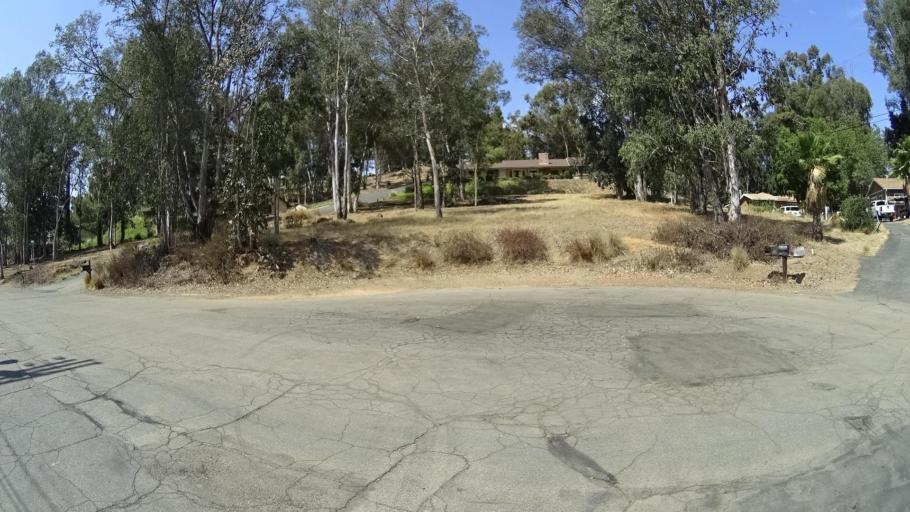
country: US
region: California
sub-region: San Diego County
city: Hidden Meadows
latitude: 33.1754
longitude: -117.0948
